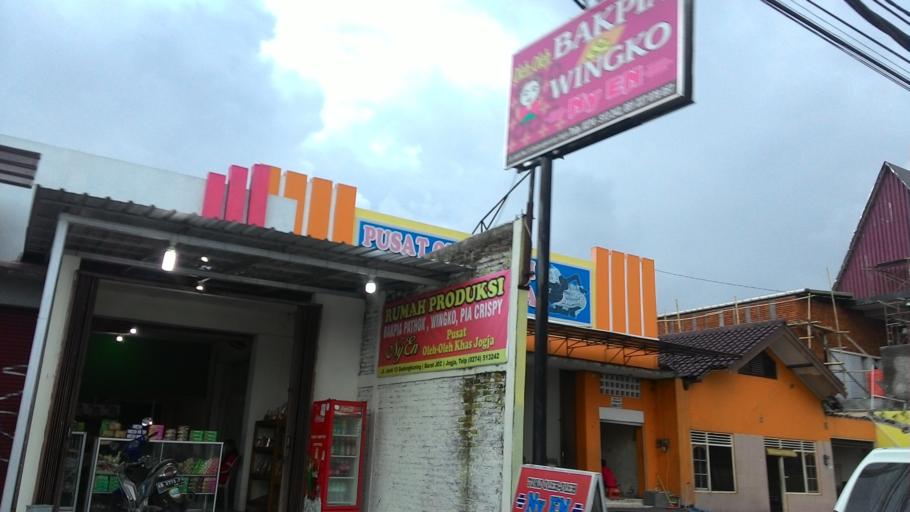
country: ID
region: Daerah Istimewa Yogyakarta
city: Yogyakarta
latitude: -7.8009
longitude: 110.4023
